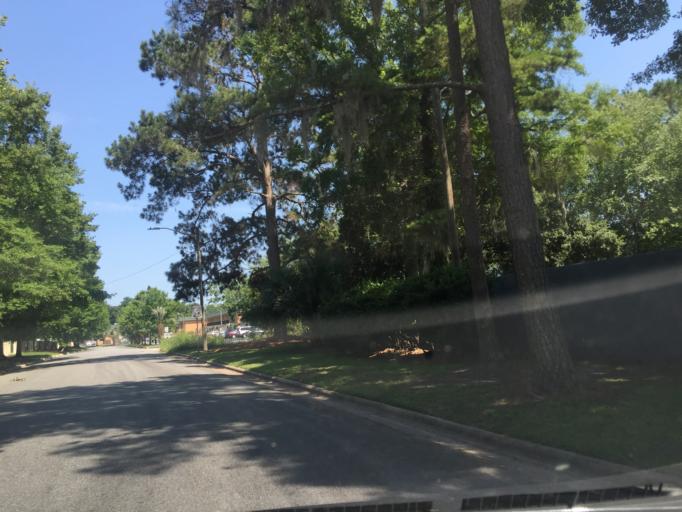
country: US
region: Georgia
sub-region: Chatham County
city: Montgomery
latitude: 31.9798
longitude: -81.1536
